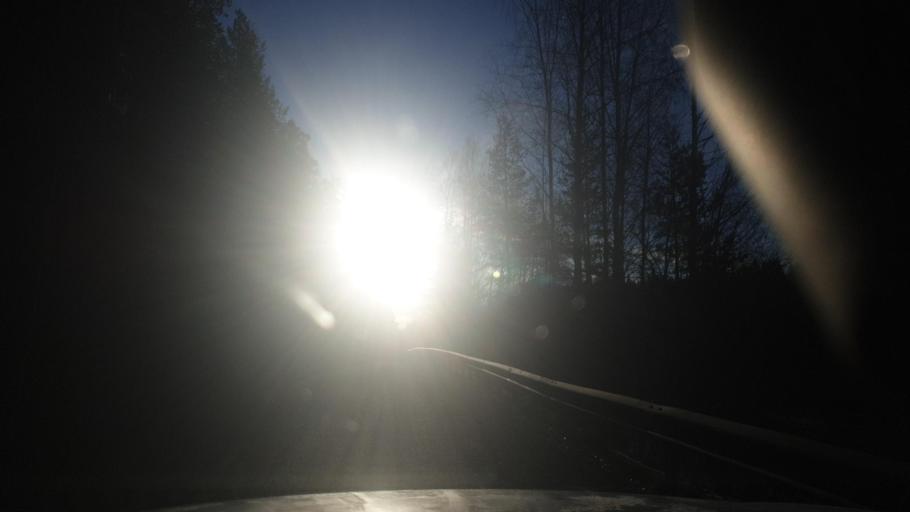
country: SE
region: Vaermland
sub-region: Sunne Kommun
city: Sunne
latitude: 59.6323
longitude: 13.0631
